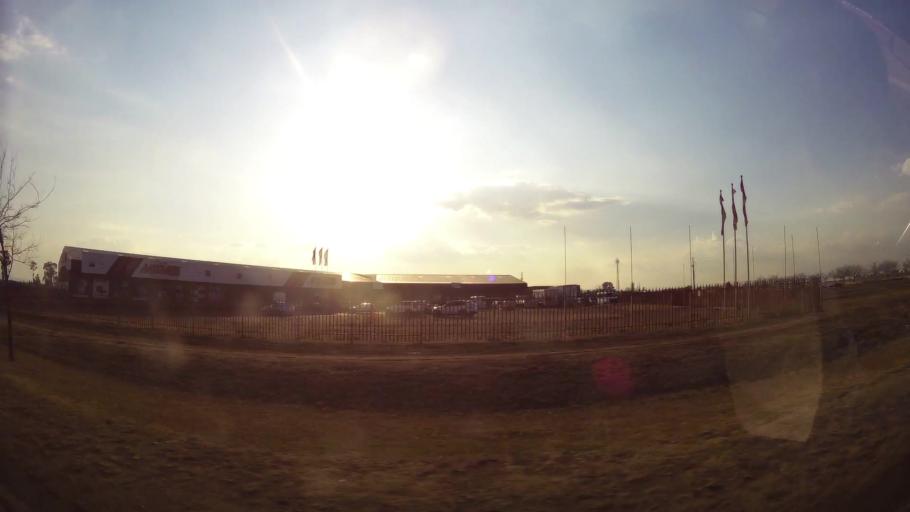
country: ZA
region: Gauteng
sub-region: Ekurhuleni Metropolitan Municipality
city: Germiston
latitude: -26.3360
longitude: 28.2297
